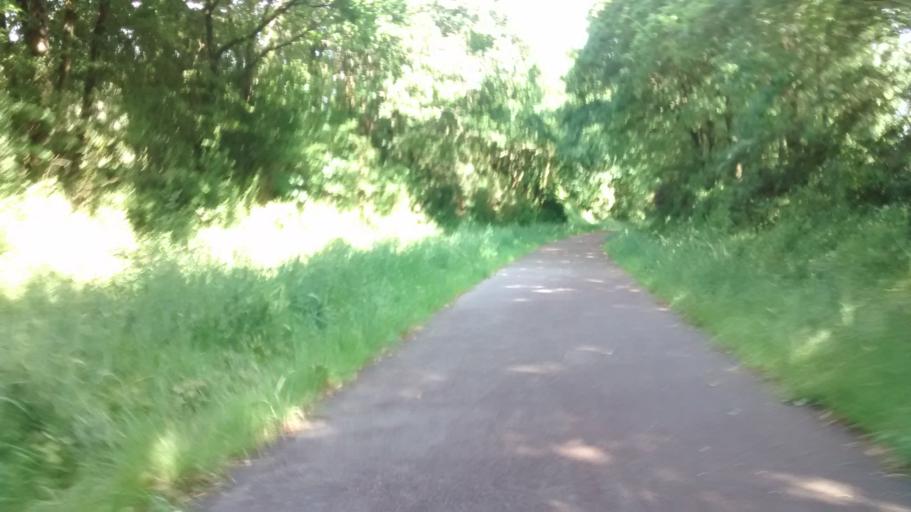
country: FR
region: Brittany
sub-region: Departement du Morbihan
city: Malestroit
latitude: 47.7867
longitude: -2.3921
